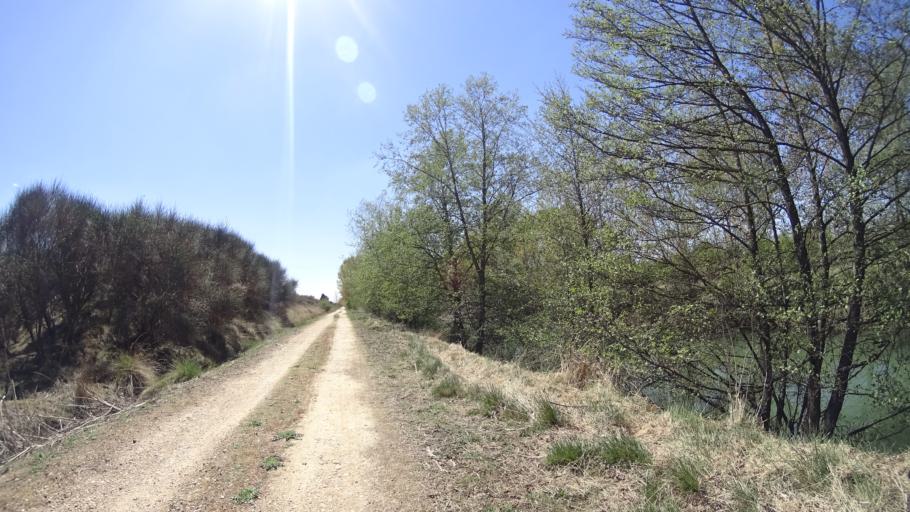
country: ES
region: Castille and Leon
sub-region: Provincia de Valladolid
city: Cubillas de Santa Marta
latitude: 41.7863
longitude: -4.6054
